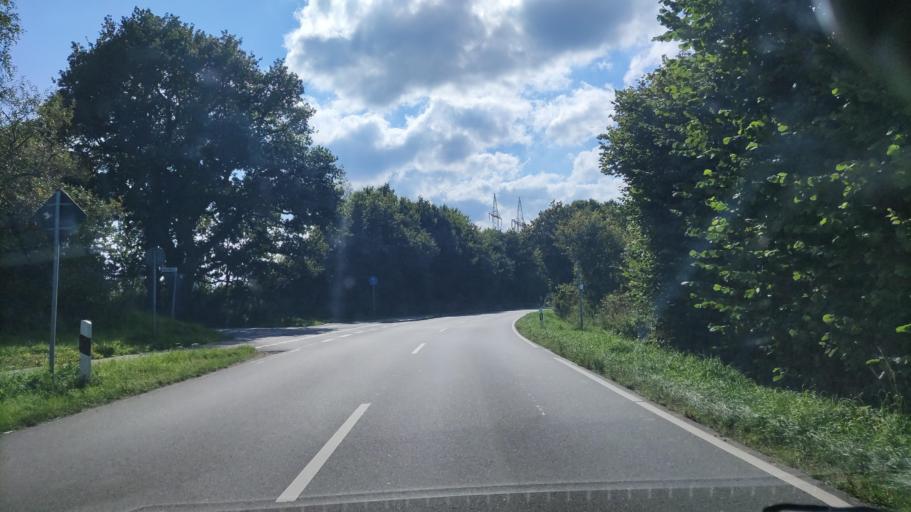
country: DE
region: Schleswig-Holstein
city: Neu Duvenstedt
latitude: 54.3706
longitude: 9.6627
